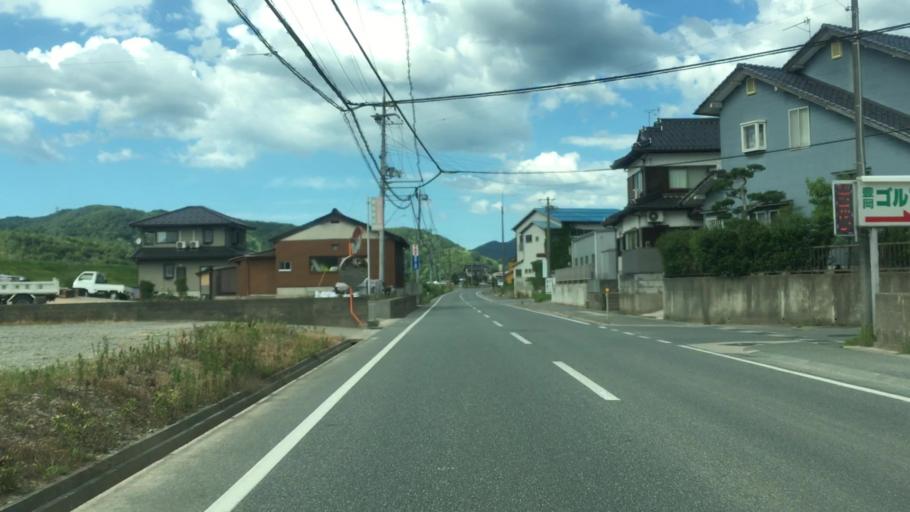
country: JP
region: Hyogo
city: Toyooka
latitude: 35.5533
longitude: 134.7931
